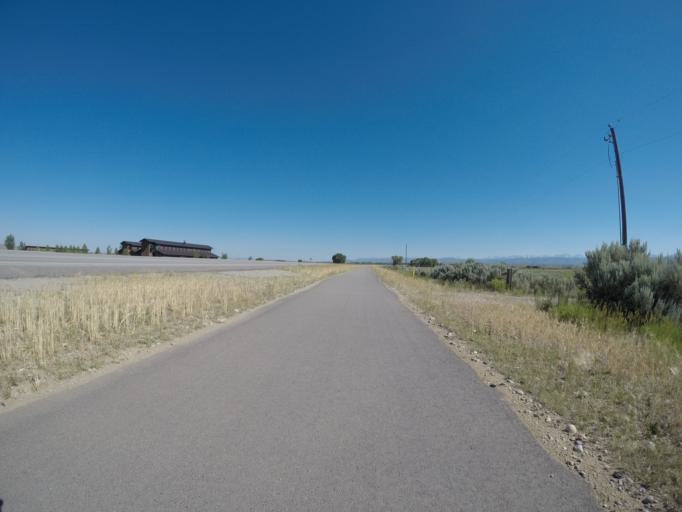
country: US
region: Wyoming
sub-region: Sublette County
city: Pinedale
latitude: 42.8303
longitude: -109.8460
